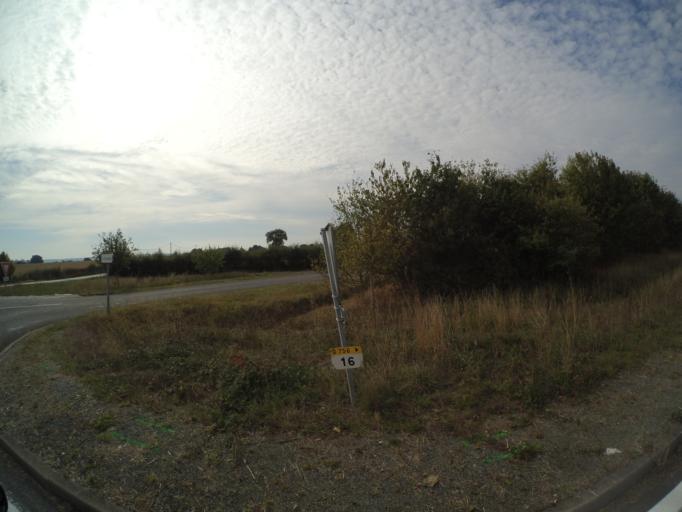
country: FR
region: Pays de la Loire
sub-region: Departement de Maine-et-Loire
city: Chemille-Melay
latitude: 47.2123
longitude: -0.7614
